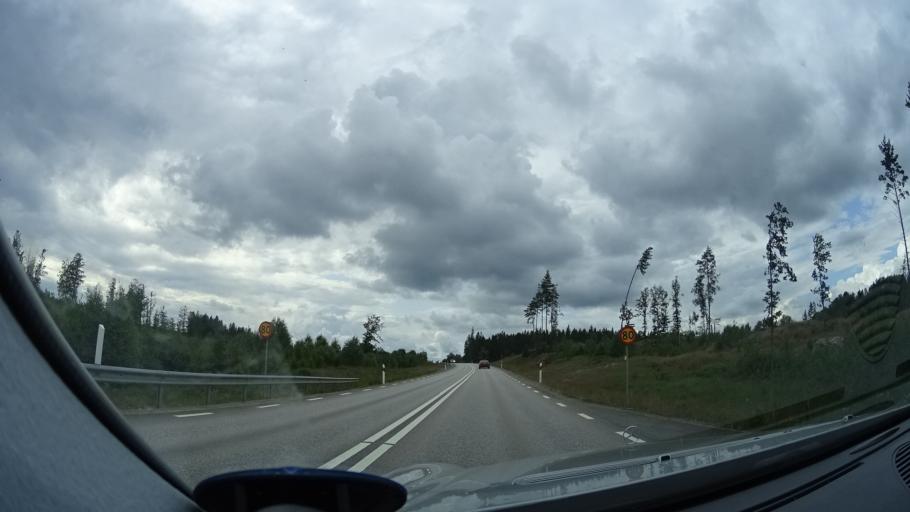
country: SE
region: Kronoberg
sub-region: Tingsryds Kommun
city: Tingsryd
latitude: 56.5032
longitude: 15.0372
